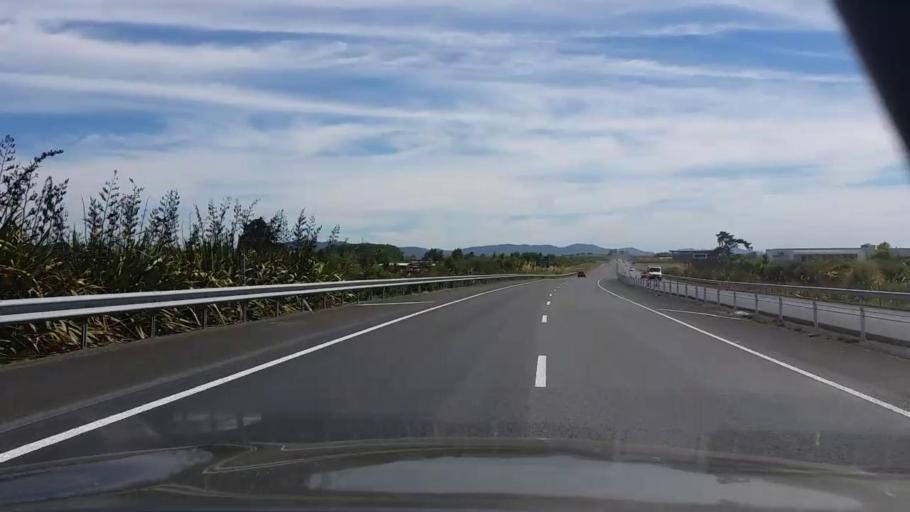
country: NZ
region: Waikato
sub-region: Hamilton City
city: Hamilton
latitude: -37.7474
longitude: 175.2156
